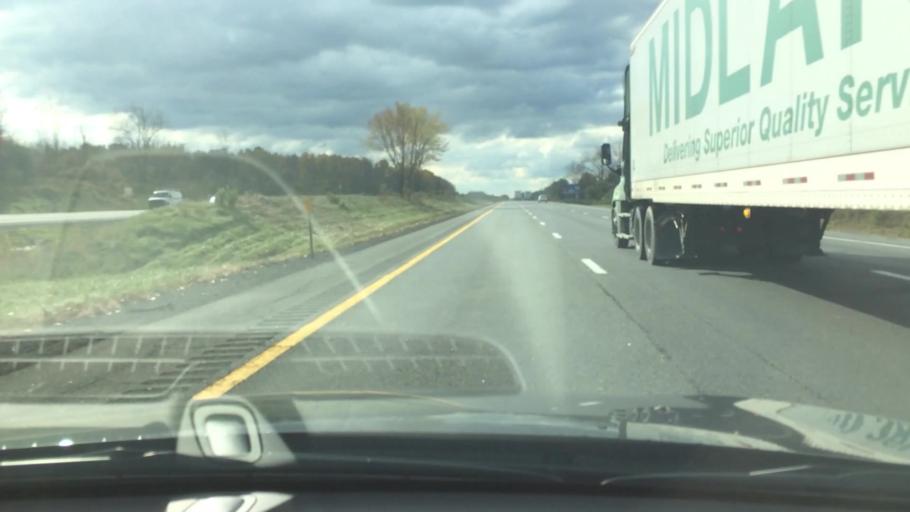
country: US
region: New York
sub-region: Saratoga County
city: Ballston Spa
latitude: 42.9823
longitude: -73.8032
